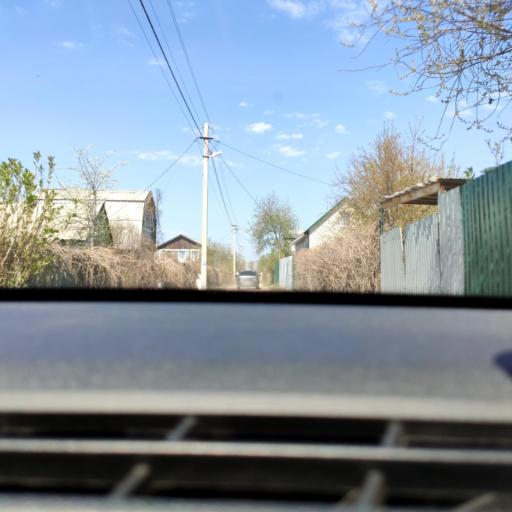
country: RU
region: Samara
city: Tol'yatti
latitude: 53.5943
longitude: 49.3010
